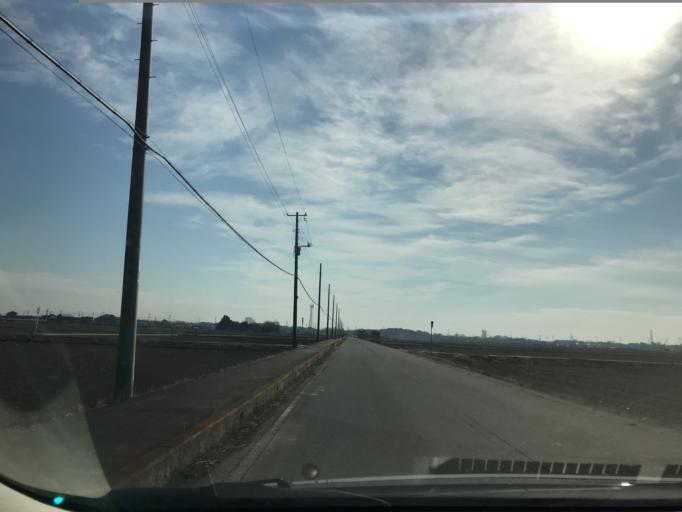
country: JP
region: Ibaraki
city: Mitsukaido
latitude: 36.0402
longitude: 140.0100
